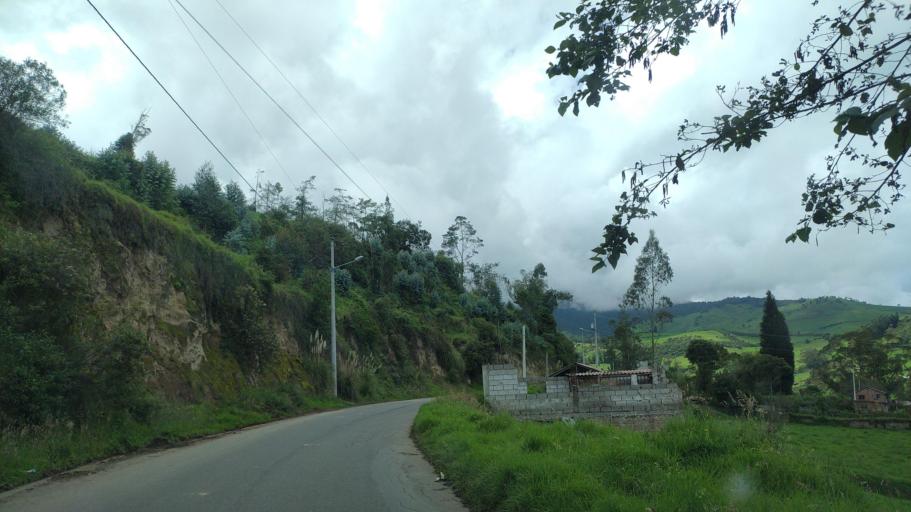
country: EC
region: Chimborazo
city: Riobamba
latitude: -1.6694
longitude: -78.5701
